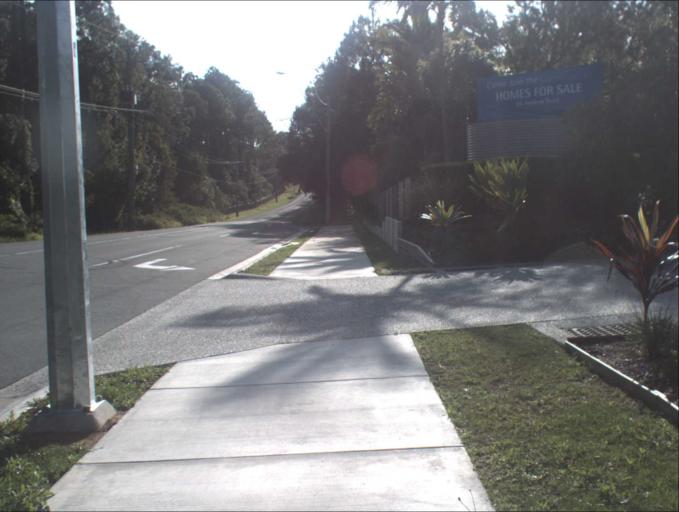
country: AU
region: Queensland
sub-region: Logan
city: Park Ridge South
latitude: -27.7113
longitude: 153.0340
